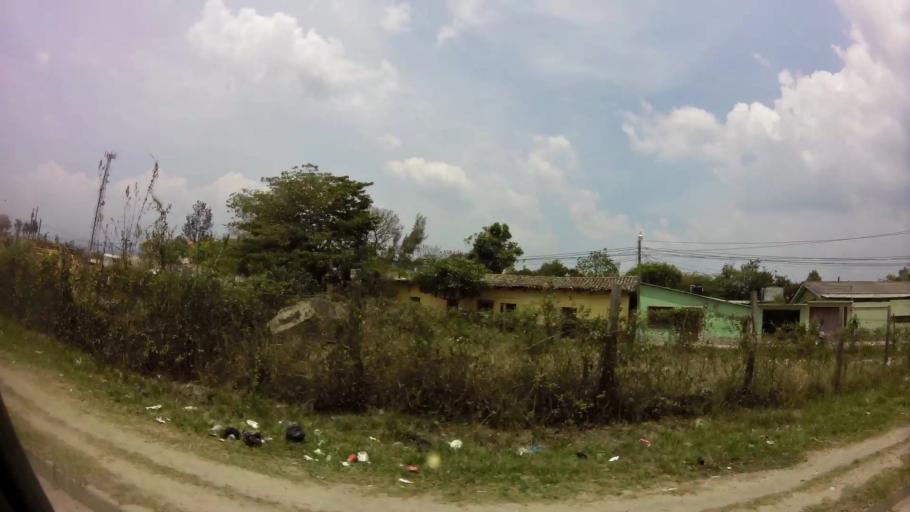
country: HN
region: Comayagua
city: Siguatepeque
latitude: 14.5987
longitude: -87.8355
